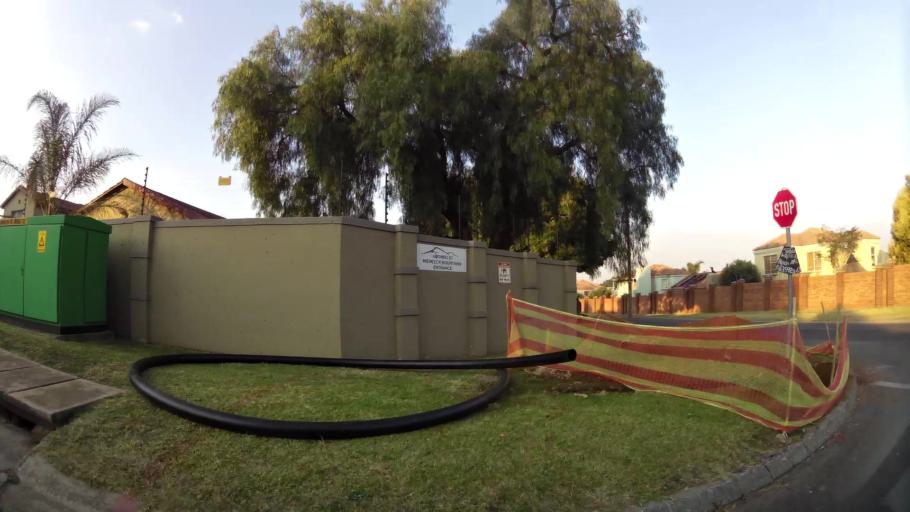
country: ZA
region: Gauteng
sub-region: City of Johannesburg Metropolitan Municipality
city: Modderfontein
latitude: -26.0830
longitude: 28.2167
